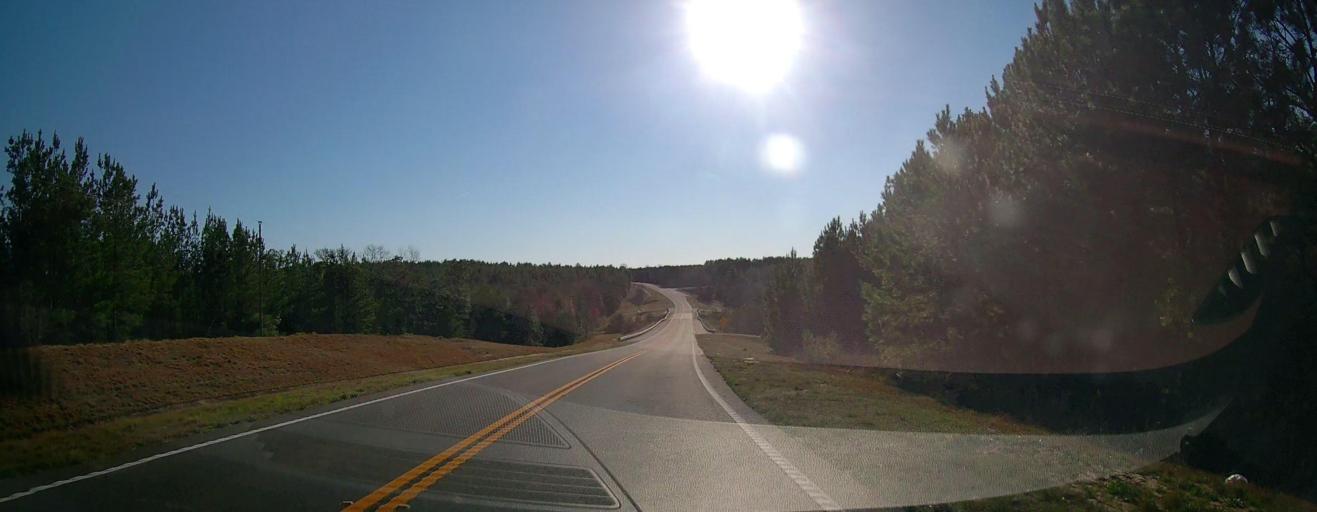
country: US
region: Georgia
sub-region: Taylor County
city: Butler
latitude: 32.5256
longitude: -84.3080
